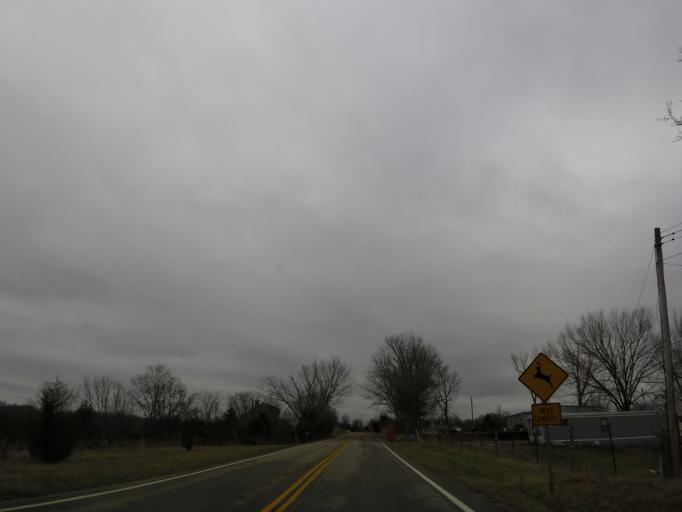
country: US
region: Kentucky
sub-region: Franklin County
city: Frankfort
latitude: 38.3424
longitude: -84.9819
